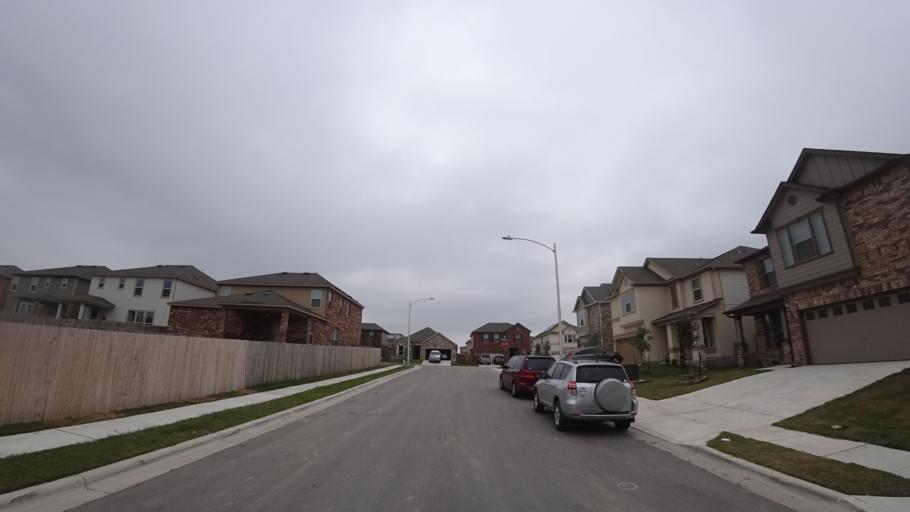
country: US
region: Texas
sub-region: Travis County
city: Pflugerville
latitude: 30.3925
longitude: -97.6477
